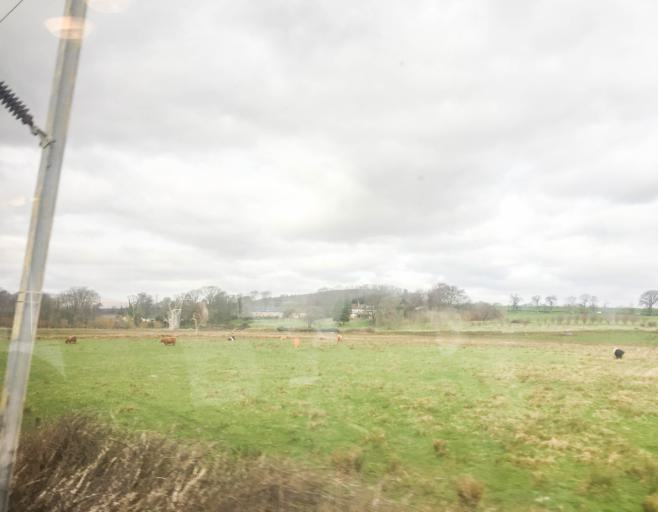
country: GB
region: Scotland
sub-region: Inverclyde
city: Port Glasgow
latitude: 55.9673
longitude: -4.6776
